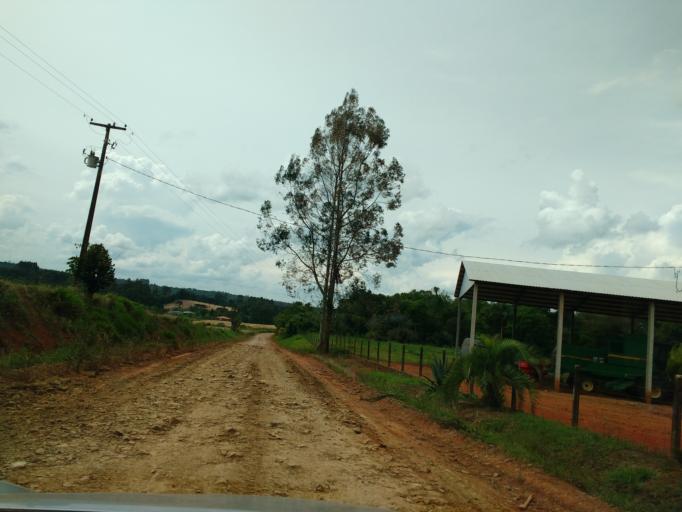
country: BR
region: Parana
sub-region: Prudentopolis
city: Prudentopolis
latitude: -25.0915
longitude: -51.0151
